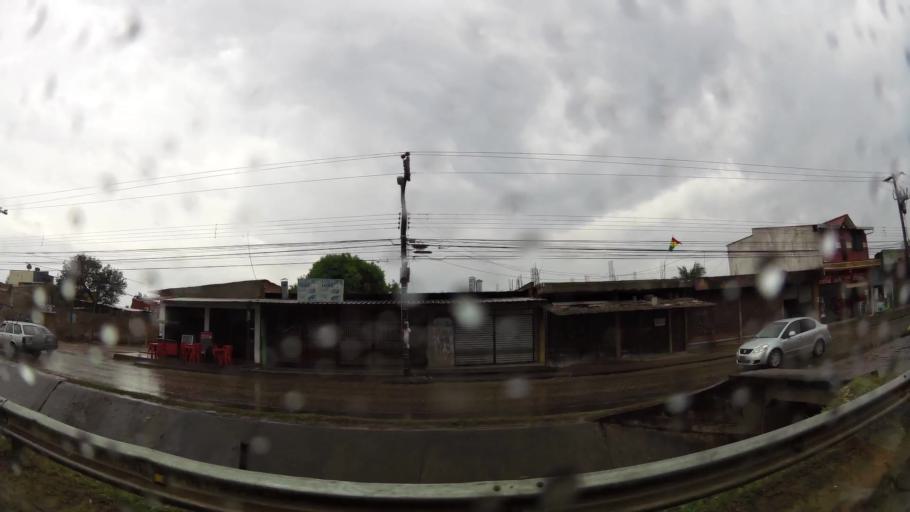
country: BO
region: Santa Cruz
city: Santa Cruz de la Sierra
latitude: -17.8037
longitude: -63.1355
